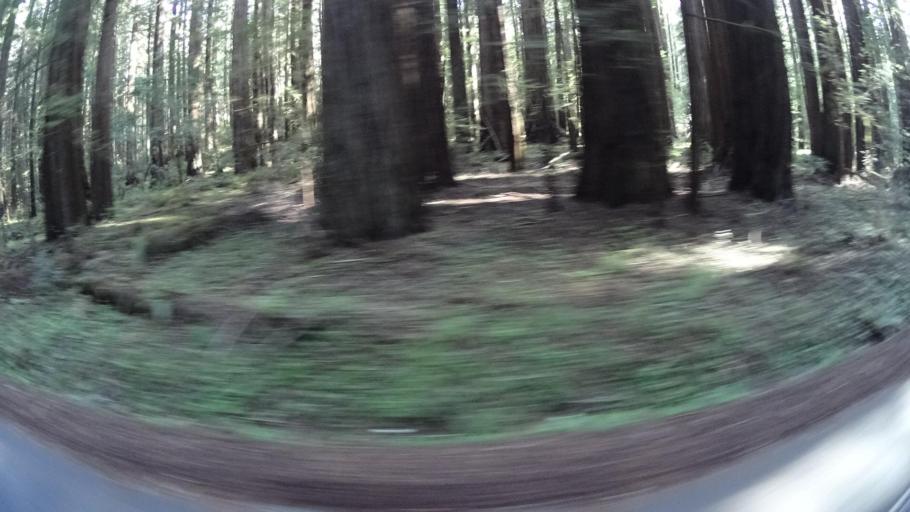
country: US
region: California
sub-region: Humboldt County
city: Rio Dell
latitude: 40.3519
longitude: -123.9940
